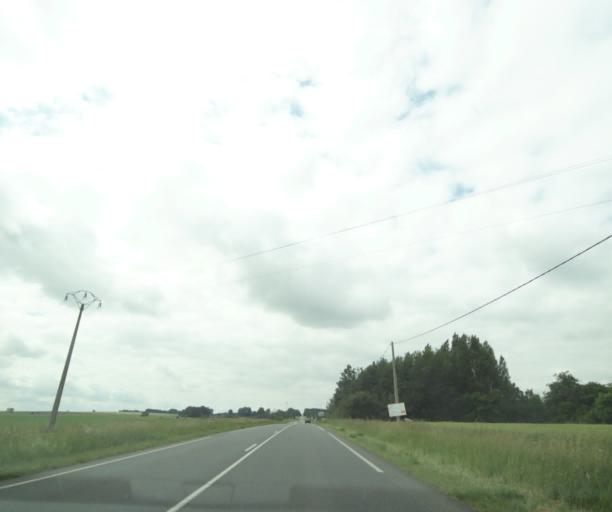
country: FR
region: Pays de la Loire
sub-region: Departement de Maine-et-Loire
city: Distre
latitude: 47.1806
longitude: -0.1334
